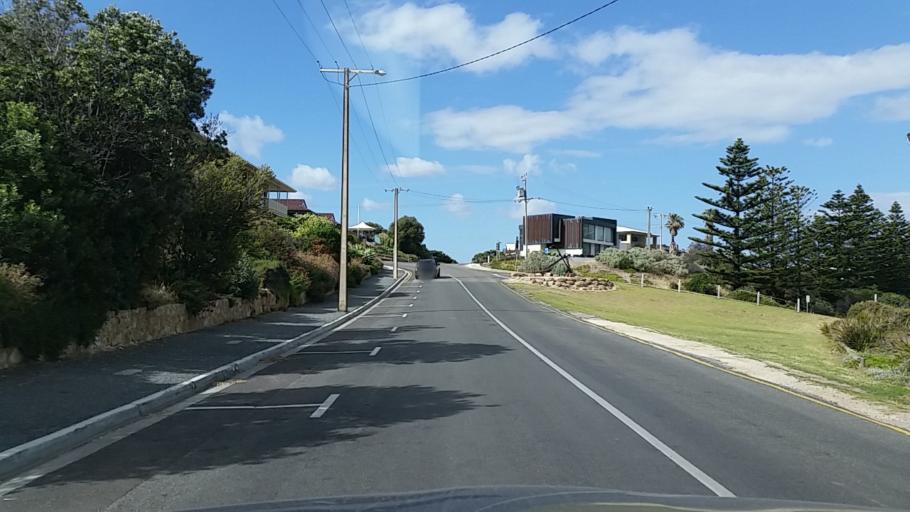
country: AU
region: South Australia
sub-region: Alexandrina
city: Port Elliot
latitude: -35.5330
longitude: 138.6842
